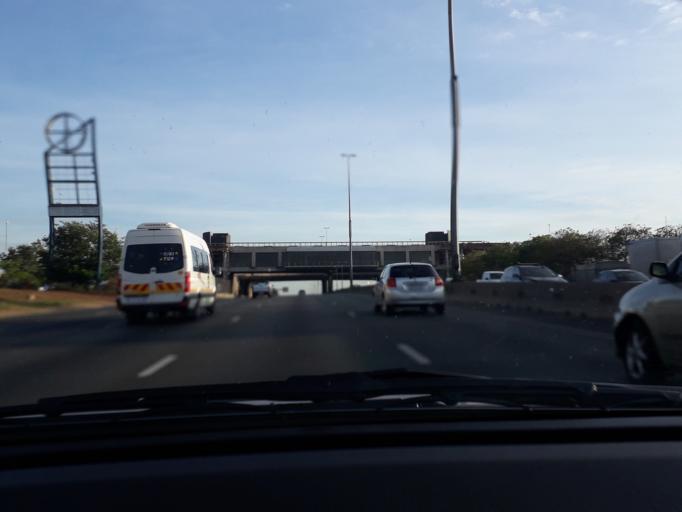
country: ZA
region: Gauteng
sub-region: City of Johannesburg Metropolitan Municipality
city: Midrand
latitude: -25.9822
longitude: 28.1256
